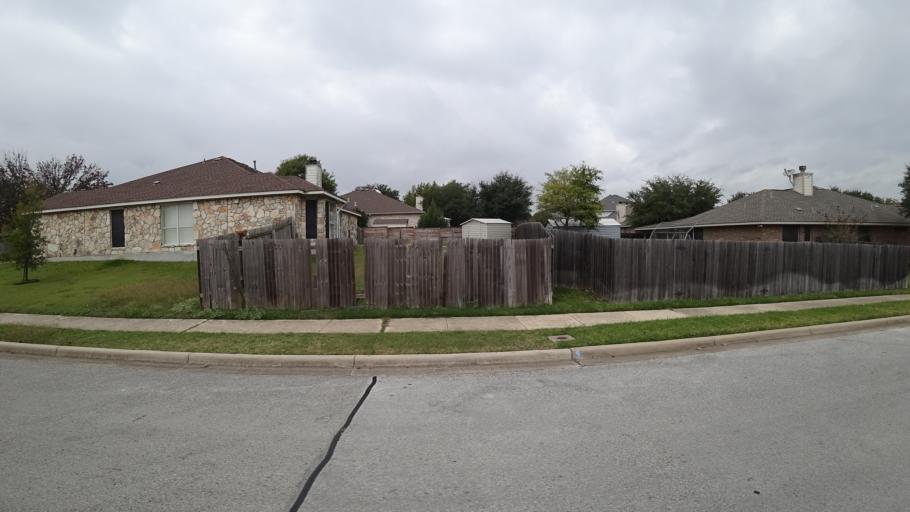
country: US
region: Texas
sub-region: Travis County
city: Pflugerville
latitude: 30.4421
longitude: -97.6040
